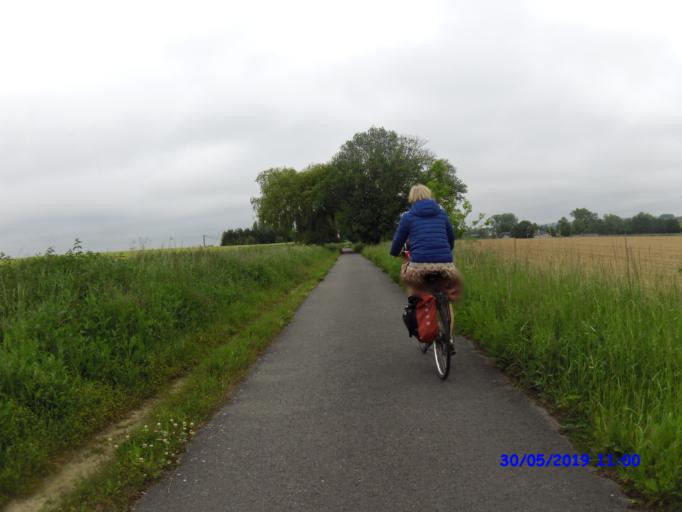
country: BE
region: Wallonia
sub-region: Province du Hainaut
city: Thuin
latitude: 50.2743
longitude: 4.3079
